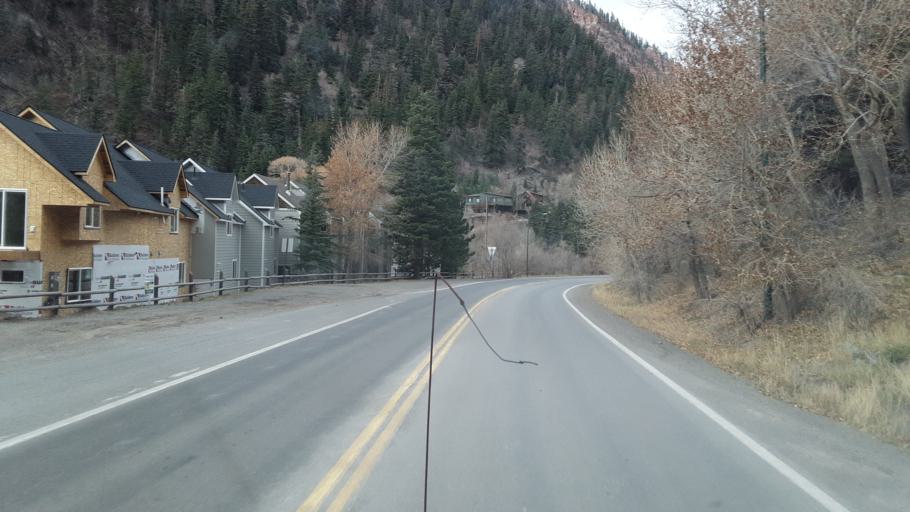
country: US
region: Colorado
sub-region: Ouray County
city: Ouray
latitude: 38.0297
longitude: -107.6727
